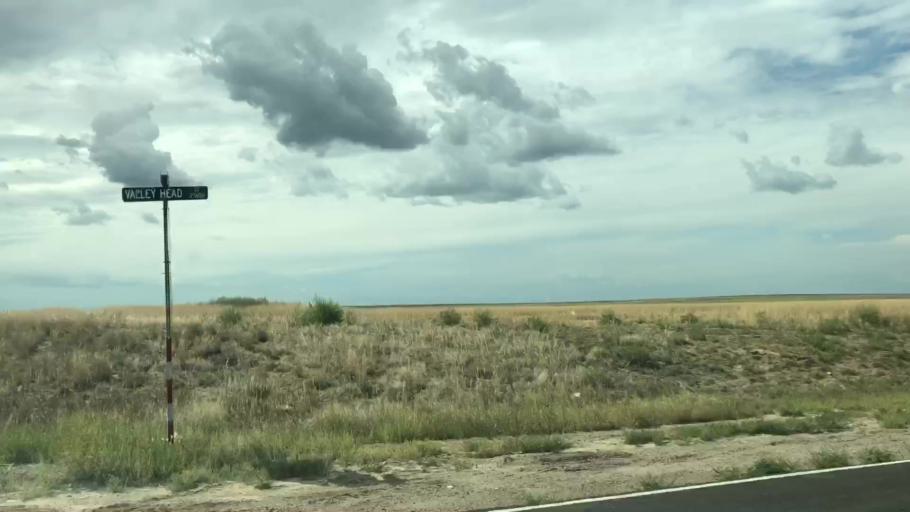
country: US
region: Colorado
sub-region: Adams County
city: Aurora
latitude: 39.7983
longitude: -104.6657
